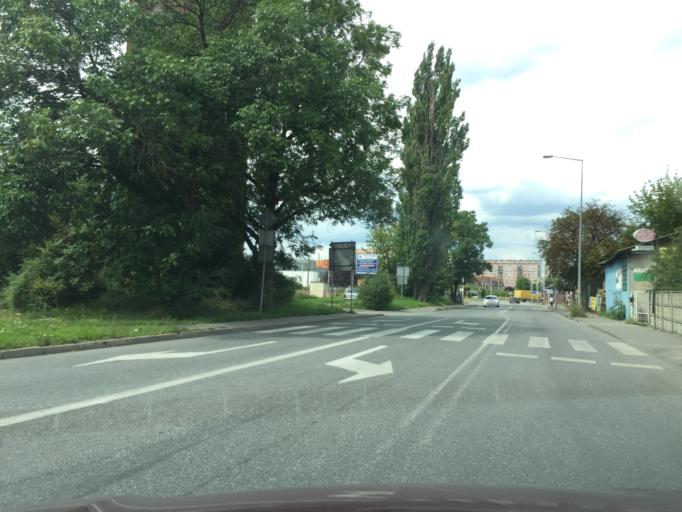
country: PL
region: Greater Poland Voivodeship
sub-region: Kalisz
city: Kalisz
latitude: 51.7429
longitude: 18.0742
